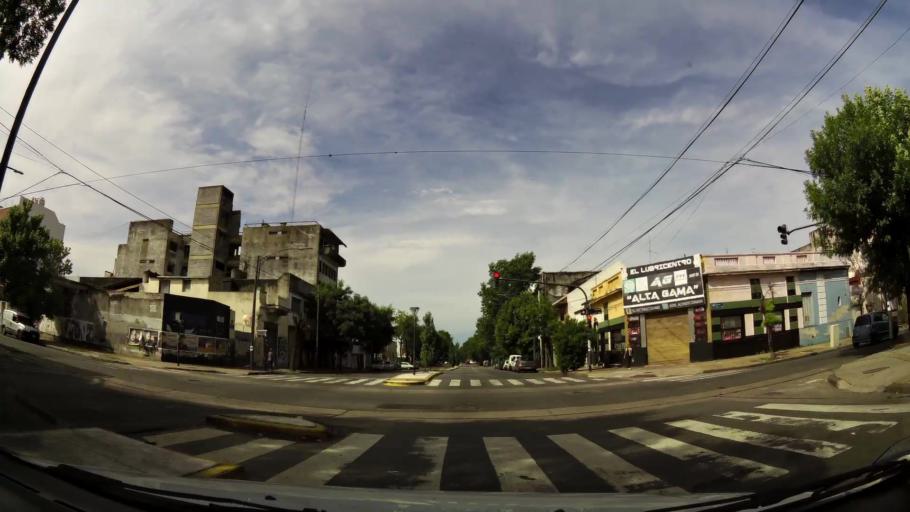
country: AR
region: Buenos Aires F.D.
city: Villa Lugano
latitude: -34.6666
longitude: -58.5051
